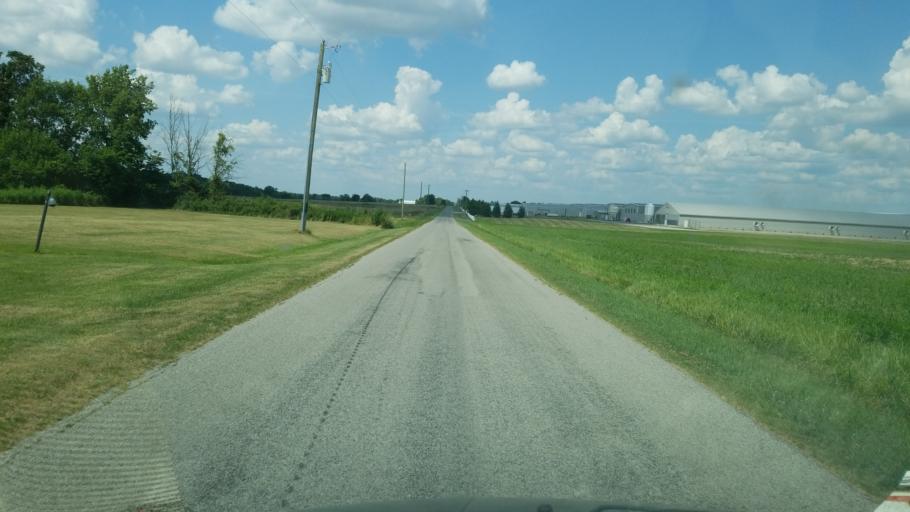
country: US
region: Ohio
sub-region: Champaign County
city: North Lewisburg
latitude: 40.3766
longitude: -83.4786
